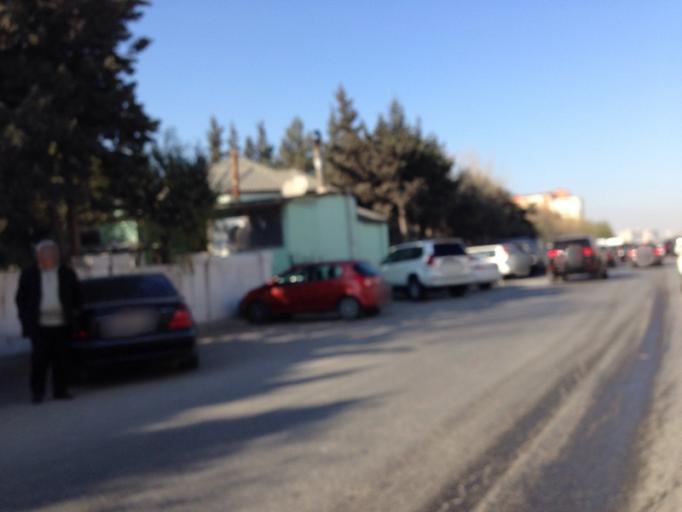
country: AZ
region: Baki
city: Baku
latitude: 40.4114
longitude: 49.8719
